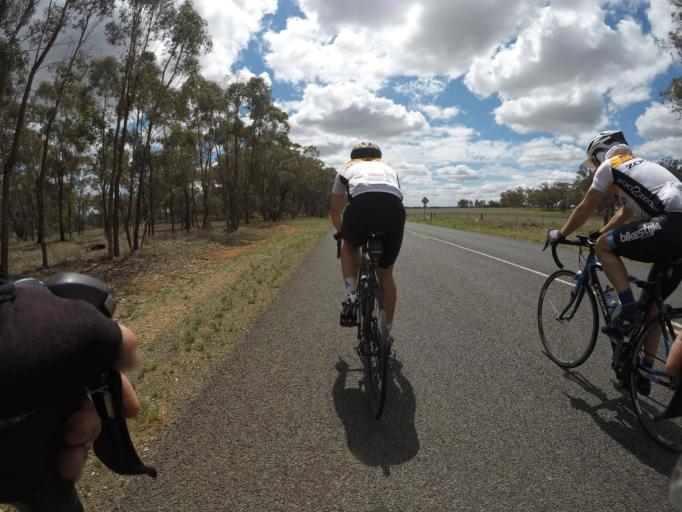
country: AU
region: New South Wales
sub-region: Dubbo Municipality
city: Dubbo
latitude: -32.4718
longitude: 148.5662
